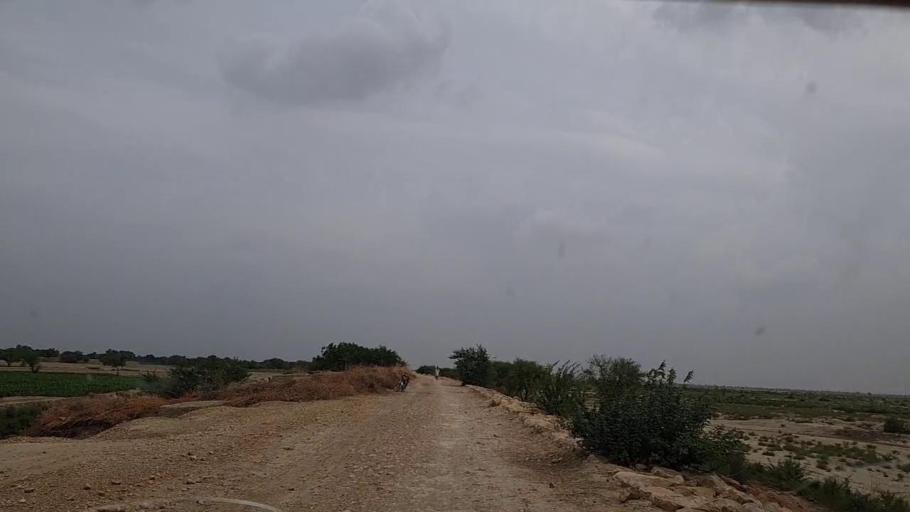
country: PK
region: Sindh
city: Johi
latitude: 26.7203
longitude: 67.5795
